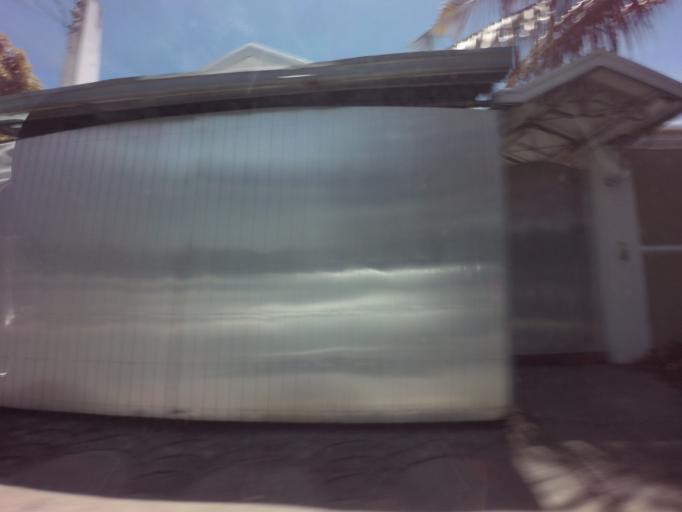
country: PH
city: Sambayanihan People's Village
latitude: 14.4897
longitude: 121.0345
